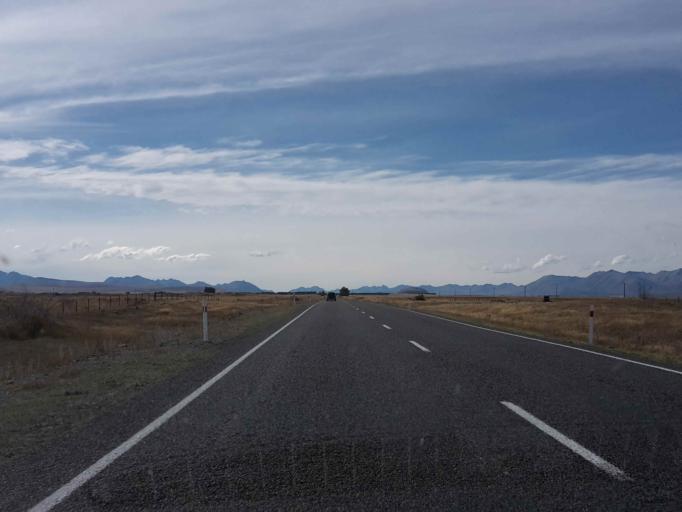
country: NZ
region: Canterbury
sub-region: Timaru District
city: Pleasant Point
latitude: -44.1513
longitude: 170.3387
